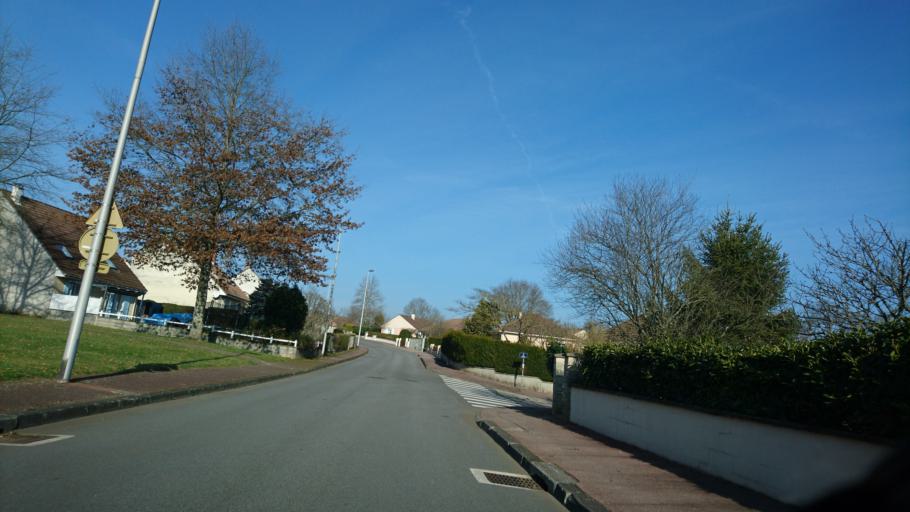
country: FR
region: Limousin
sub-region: Departement de la Haute-Vienne
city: Rilhac-Rancon
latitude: 45.8805
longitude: 1.3025
